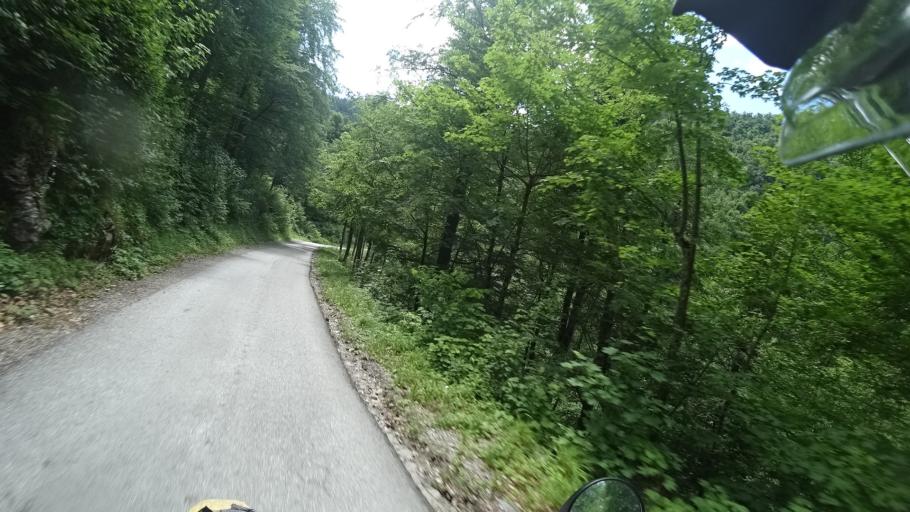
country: SI
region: Osilnica
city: Osilnica
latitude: 45.5049
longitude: 14.6300
